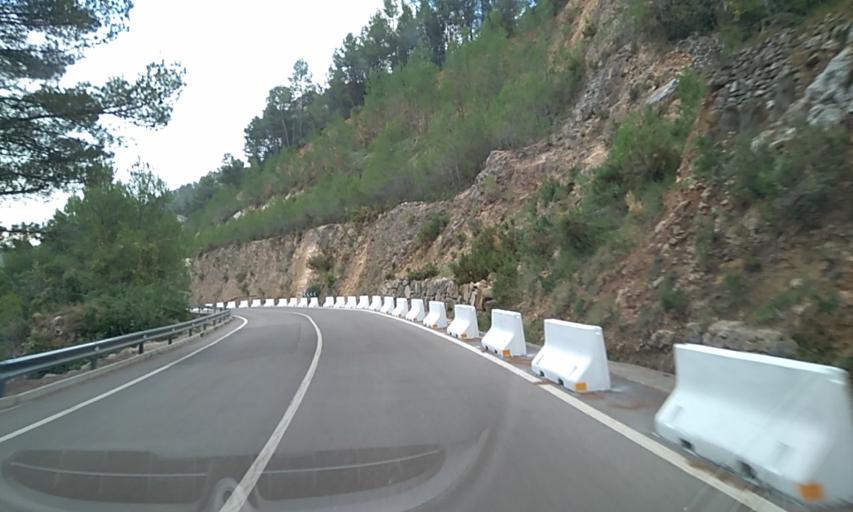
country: ES
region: Valencia
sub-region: Provincia de Castello
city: Montanejos
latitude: 40.0748
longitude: -0.5379
